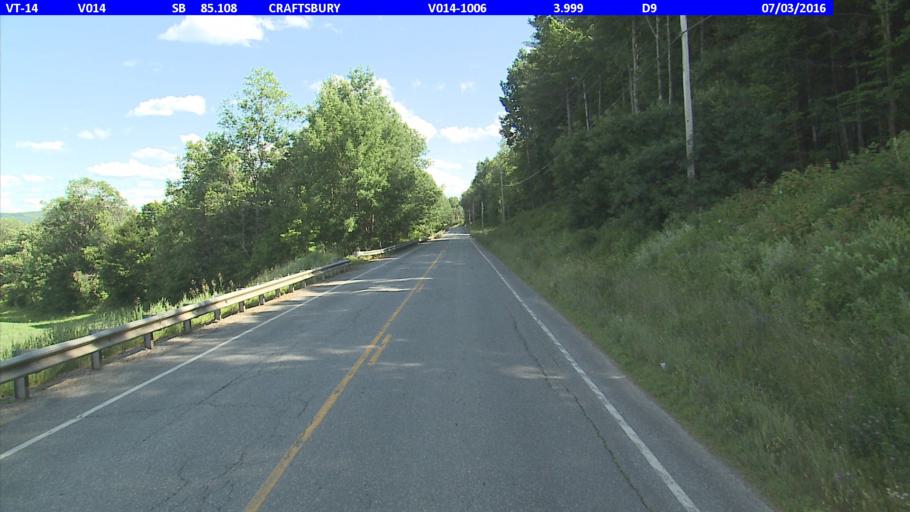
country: US
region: Vermont
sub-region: Caledonia County
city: Hardwick
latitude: 44.6485
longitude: -72.4045
